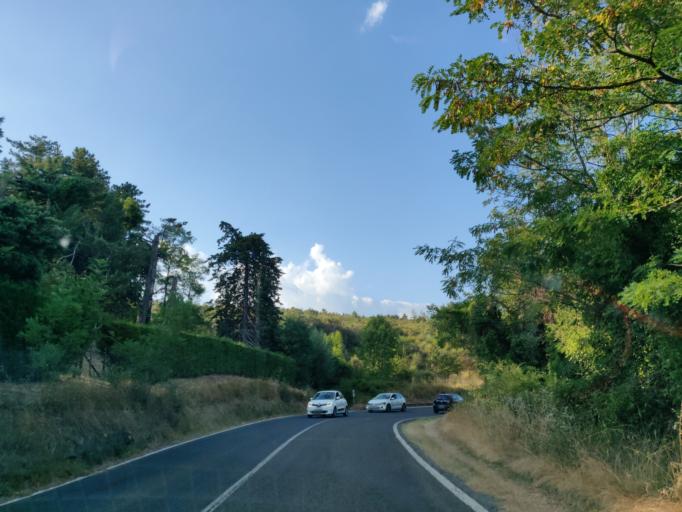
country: IT
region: Tuscany
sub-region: Provincia di Siena
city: Abbadia San Salvatore
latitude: 42.8681
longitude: 11.6814
